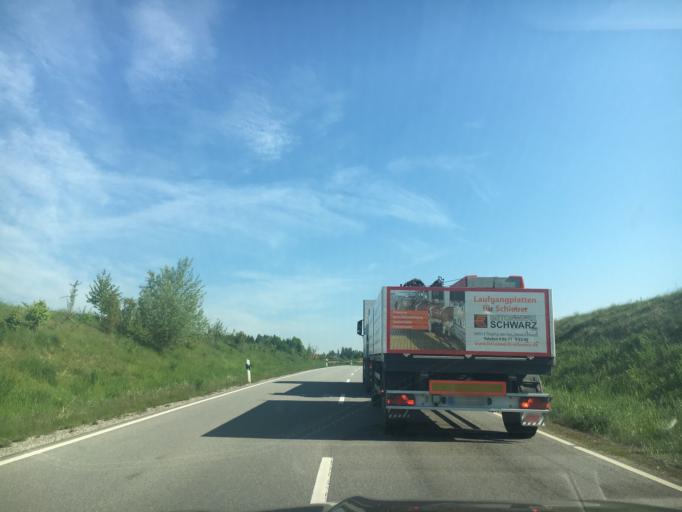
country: DE
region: Bavaria
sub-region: Upper Bavaria
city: Neumarkt-Sankt Veit
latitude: 48.3556
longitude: 12.4893
